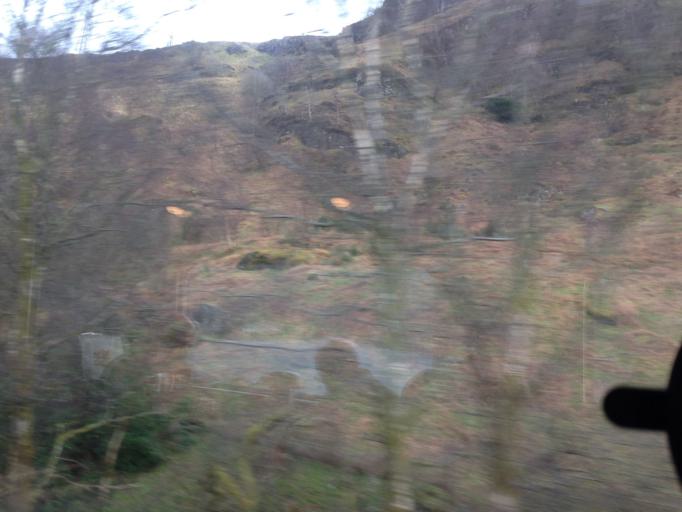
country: GB
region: Scotland
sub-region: Argyll and Bute
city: Garelochhead
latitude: 56.1753
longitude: -4.7748
